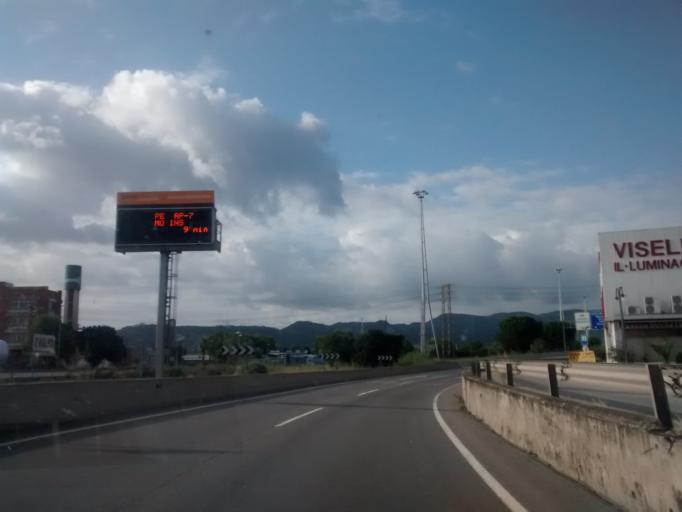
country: ES
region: Catalonia
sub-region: Provincia de Barcelona
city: Martorell
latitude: 41.4926
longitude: 1.9122
